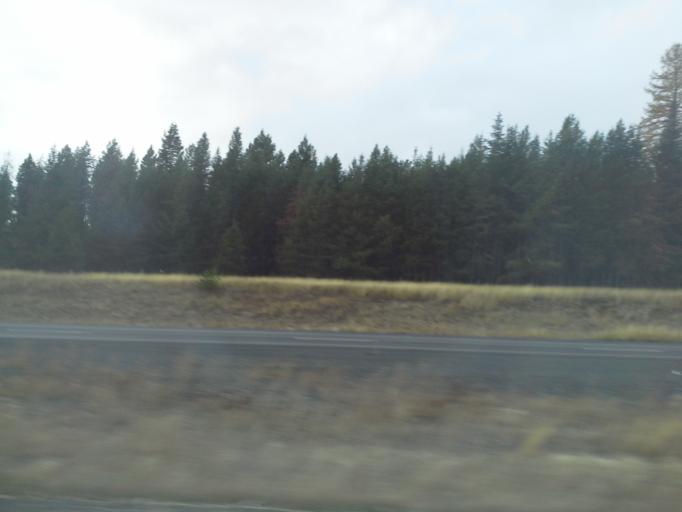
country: US
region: Oregon
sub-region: Umatilla County
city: Mission
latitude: 45.4999
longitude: -118.4195
